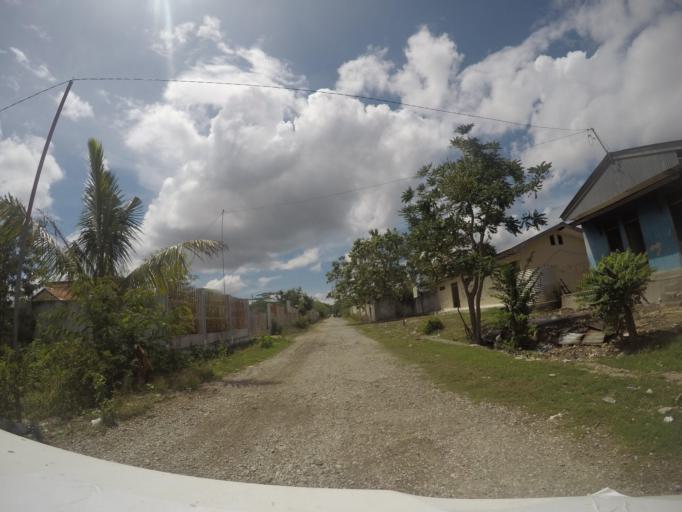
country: TL
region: Baucau
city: Baucau
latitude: -8.4711
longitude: 126.4571
